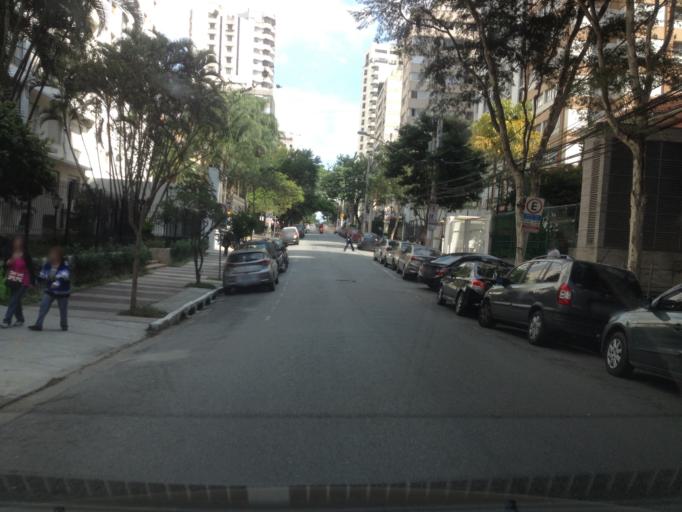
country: BR
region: Sao Paulo
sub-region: Sao Paulo
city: Sao Paulo
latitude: -23.5702
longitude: -46.6483
